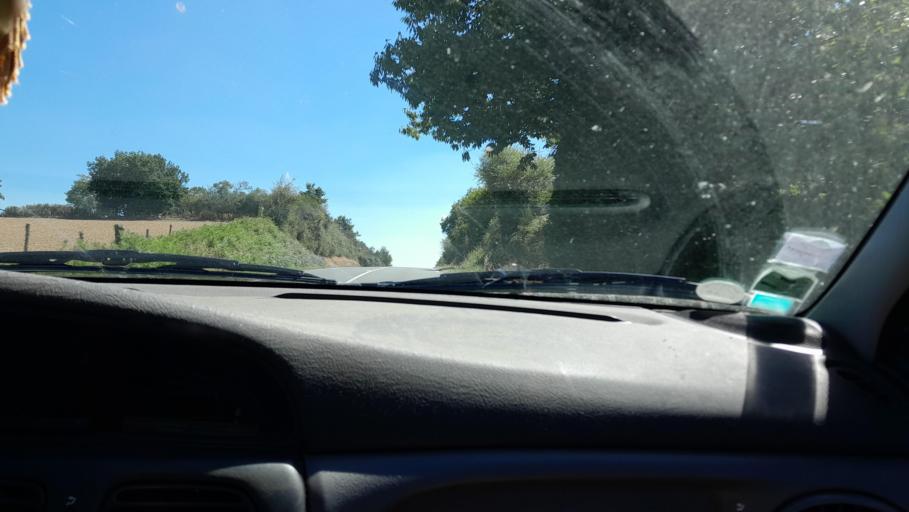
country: FR
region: Pays de la Loire
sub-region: Departement de la Loire-Atlantique
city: Saint-Mars-la-Jaille
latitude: 47.5460
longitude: -1.1855
